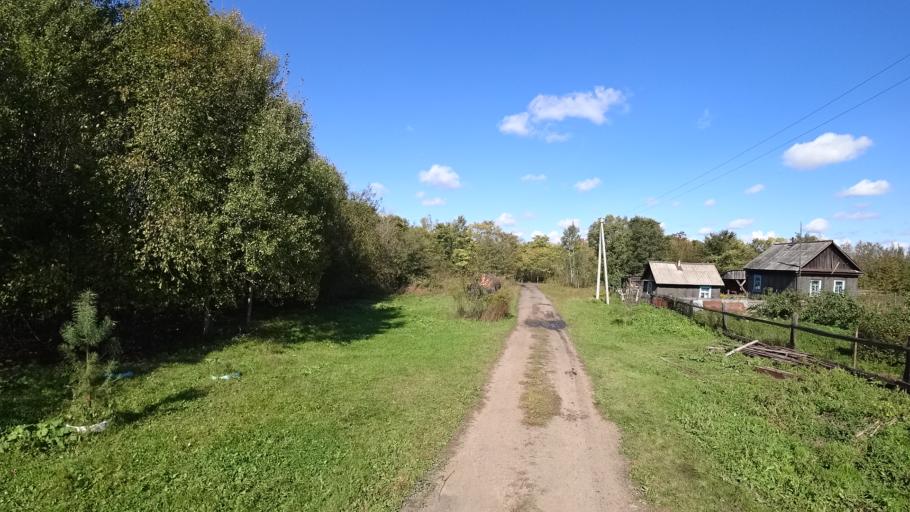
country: RU
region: Amur
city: Arkhara
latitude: 49.4003
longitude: 130.1266
